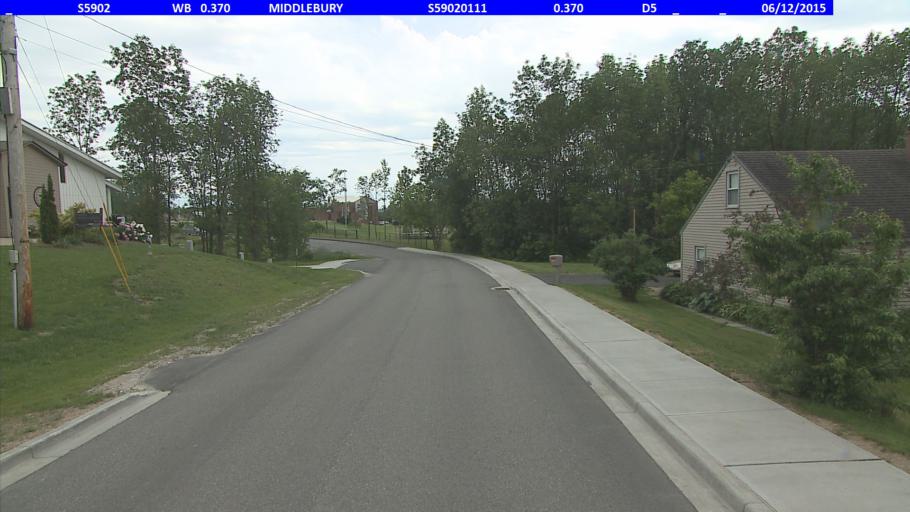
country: US
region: Vermont
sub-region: Addison County
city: Middlebury (village)
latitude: 44.0099
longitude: -73.1655
